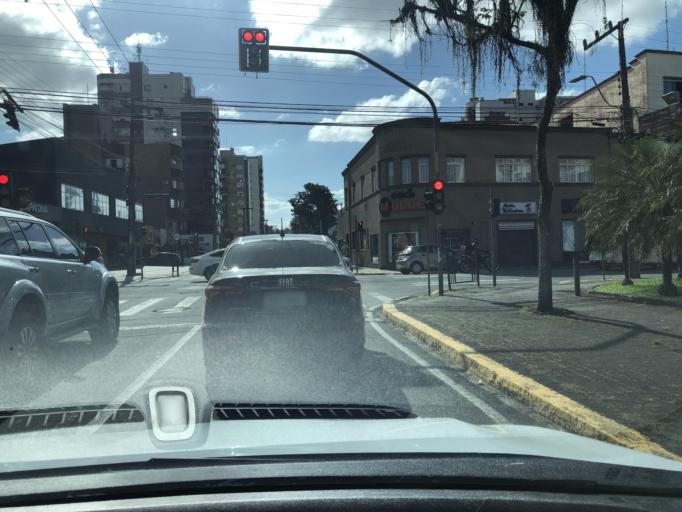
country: BR
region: Santa Catarina
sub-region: Joinville
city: Joinville
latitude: -26.2969
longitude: -48.8474
